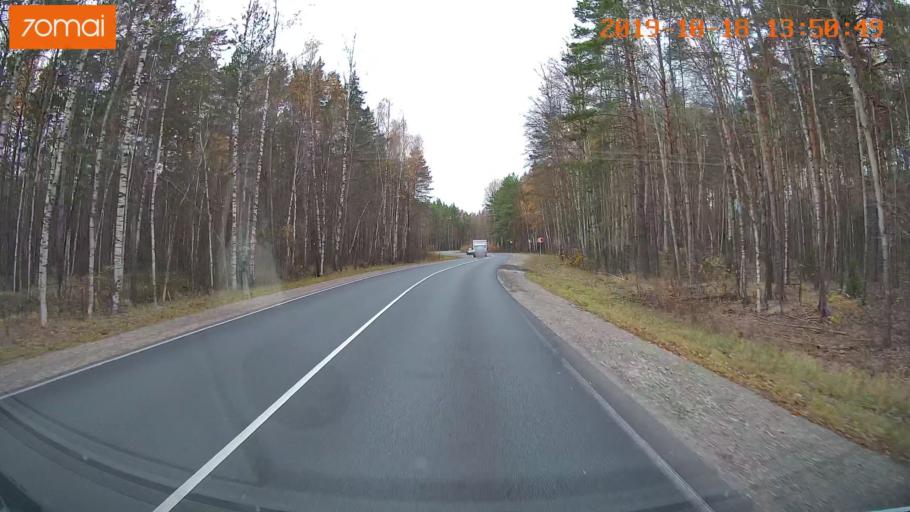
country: RU
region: Moskovskaya
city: Radovitskiy
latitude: 55.0108
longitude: 39.9662
